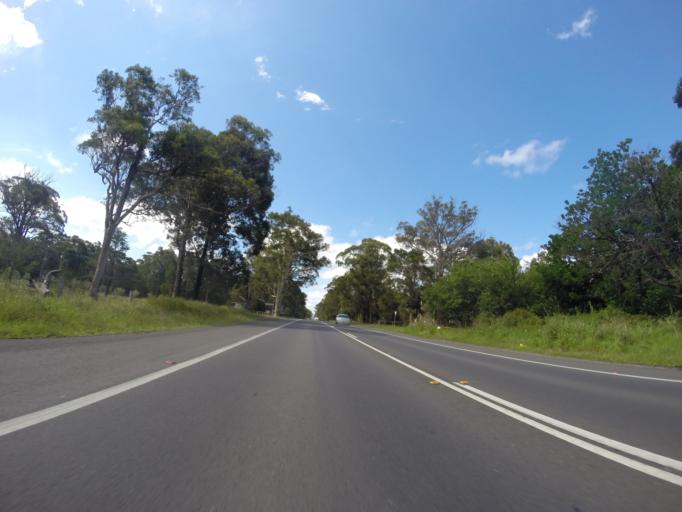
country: AU
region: New South Wales
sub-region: Shoalhaven Shire
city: Falls Creek
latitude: -35.0035
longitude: 150.5828
